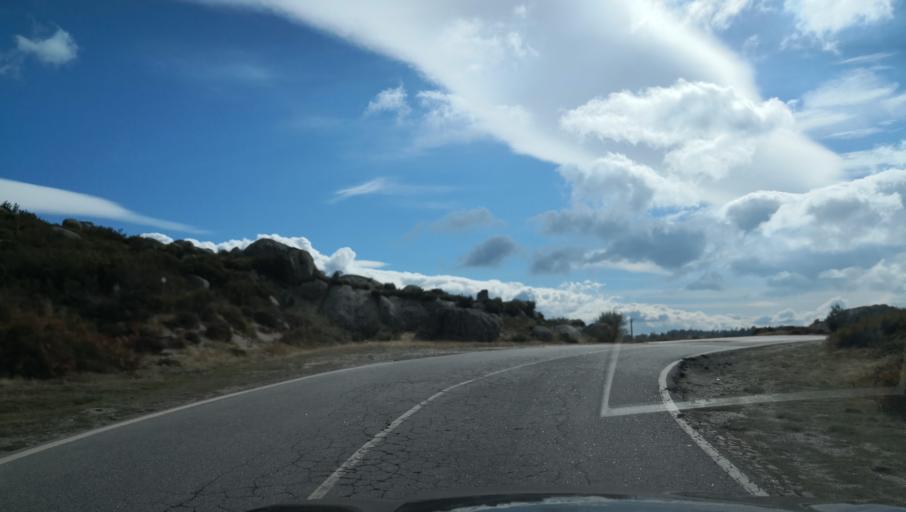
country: PT
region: Vila Real
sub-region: Vila Real
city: Vila Real
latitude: 41.3593
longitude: -7.7964
